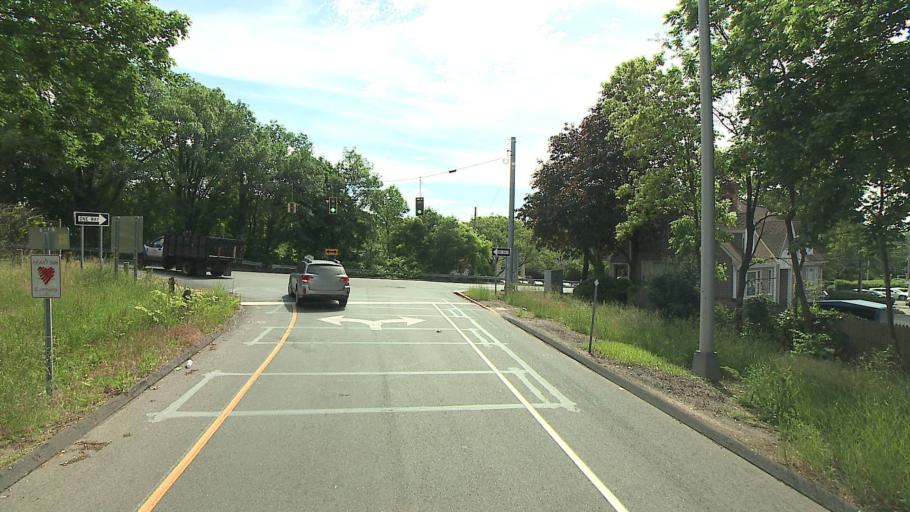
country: US
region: Connecticut
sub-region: Fairfield County
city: Darien
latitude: 41.0678
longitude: -73.4907
